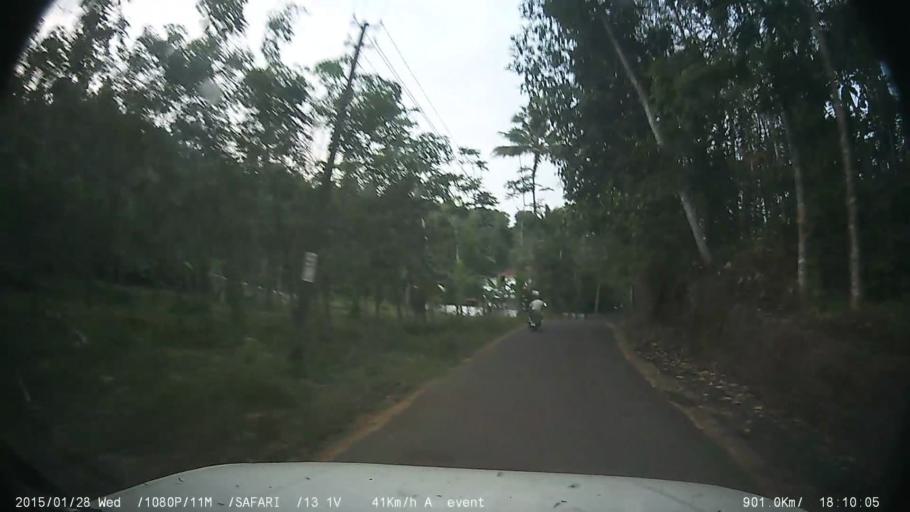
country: IN
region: Kerala
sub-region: Kottayam
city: Palackattumala
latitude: 9.7443
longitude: 76.5706
